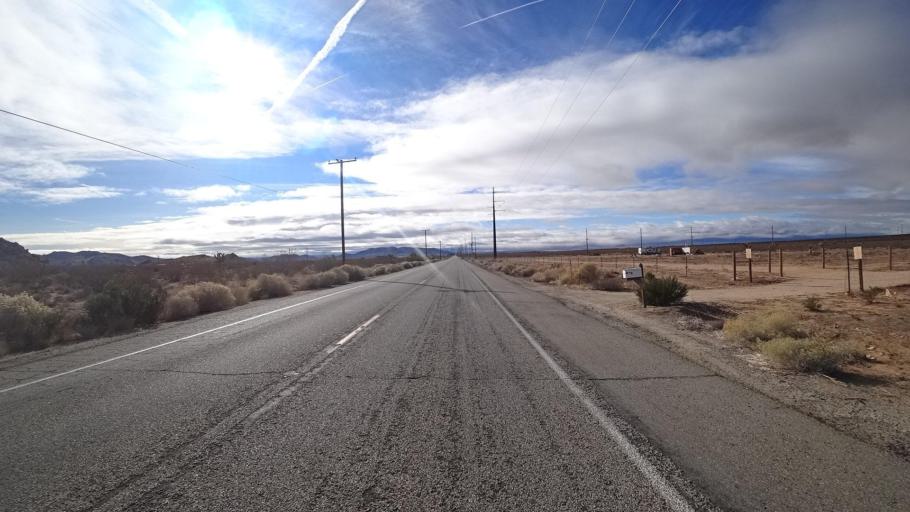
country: US
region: California
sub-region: Kern County
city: Mojave
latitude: 34.9530
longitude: -118.2918
